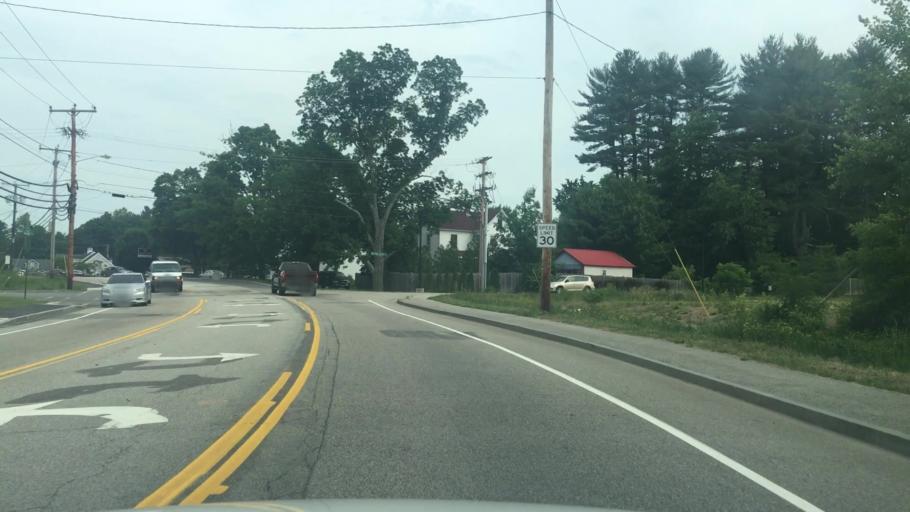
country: US
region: New Hampshire
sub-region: Rockingham County
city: Exeter
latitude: 42.9876
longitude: -70.9651
